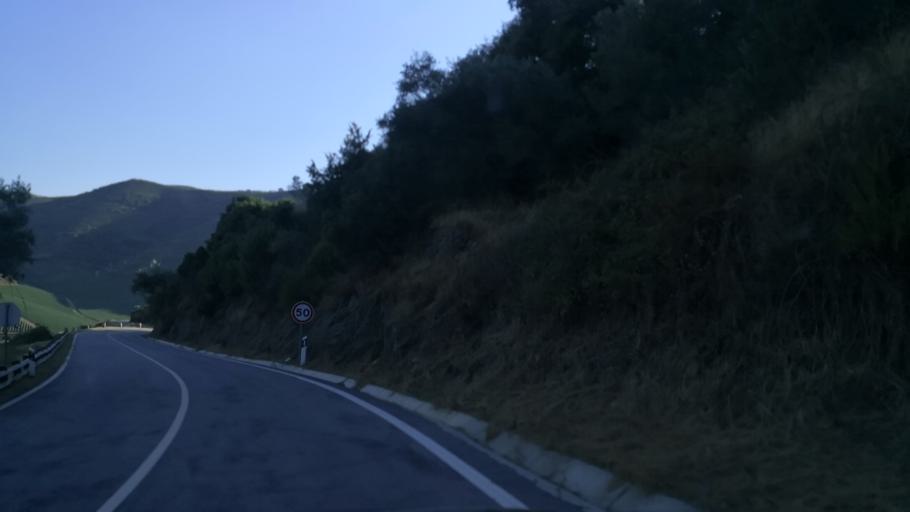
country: PT
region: Viseu
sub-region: Sao Joao da Pesqueira
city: Sao Joao da Pesqueira
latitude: 41.2169
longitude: -7.4296
